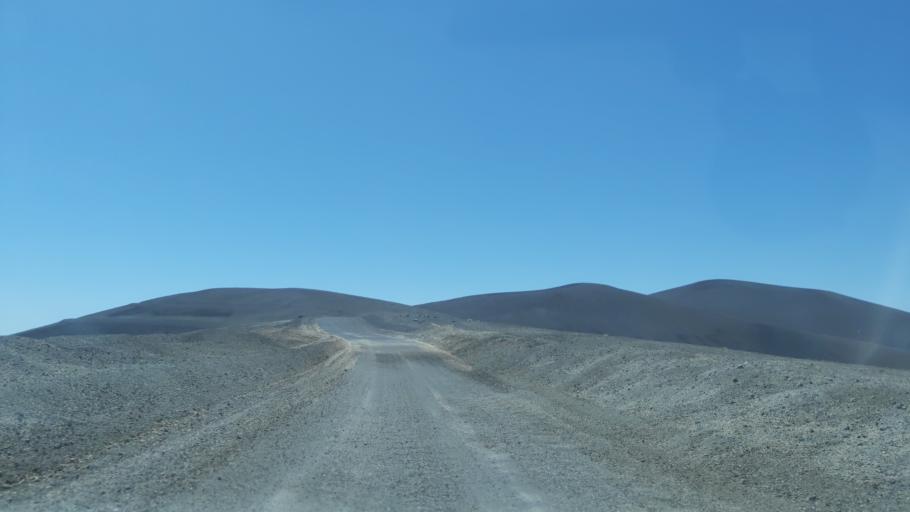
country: CL
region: Araucania
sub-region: Provincia de Cautin
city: Vilcun
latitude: -38.3758
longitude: -71.5403
